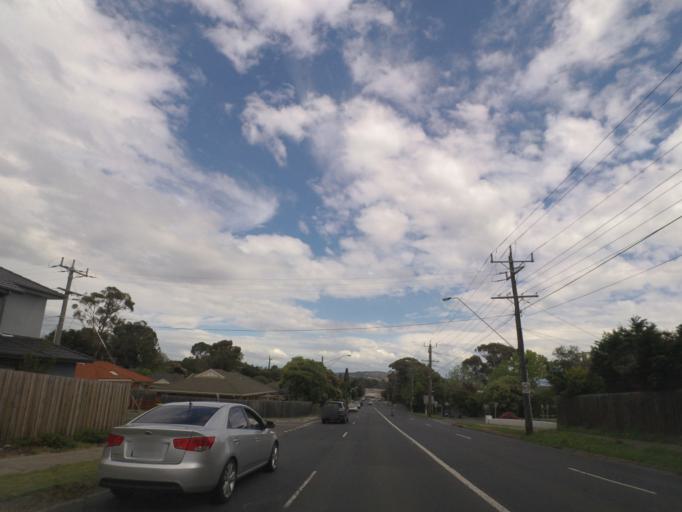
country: AU
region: Victoria
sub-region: Knox
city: Ferntree Gully
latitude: -37.8828
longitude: 145.2845
